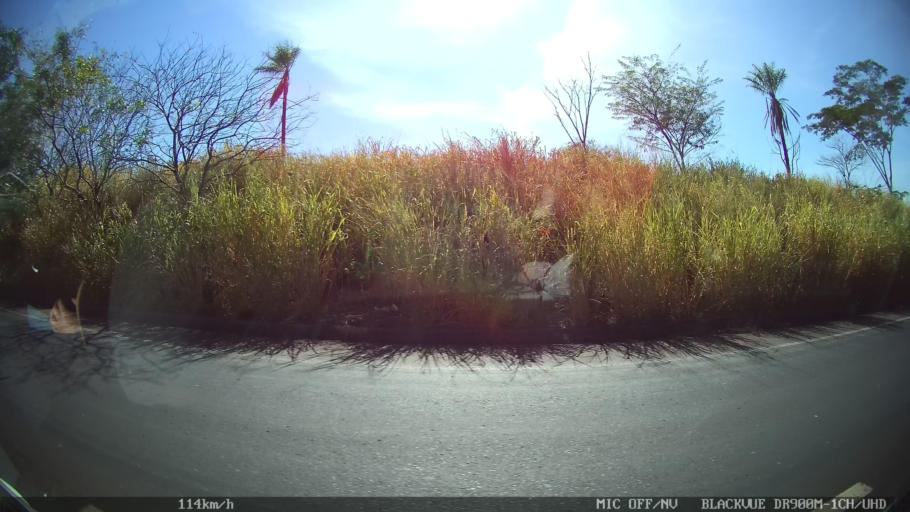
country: BR
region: Sao Paulo
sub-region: Olimpia
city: Olimpia
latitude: -20.6204
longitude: -48.7668
